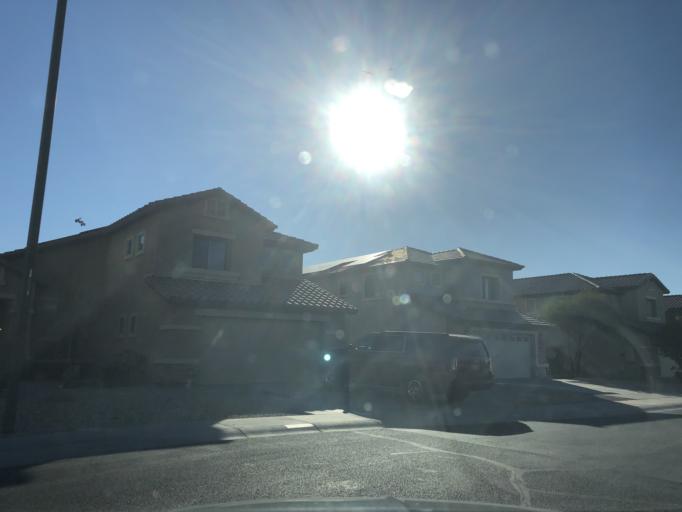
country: US
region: Arizona
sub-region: Maricopa County
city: Buckeye
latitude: 33.4267
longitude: -112.6044
